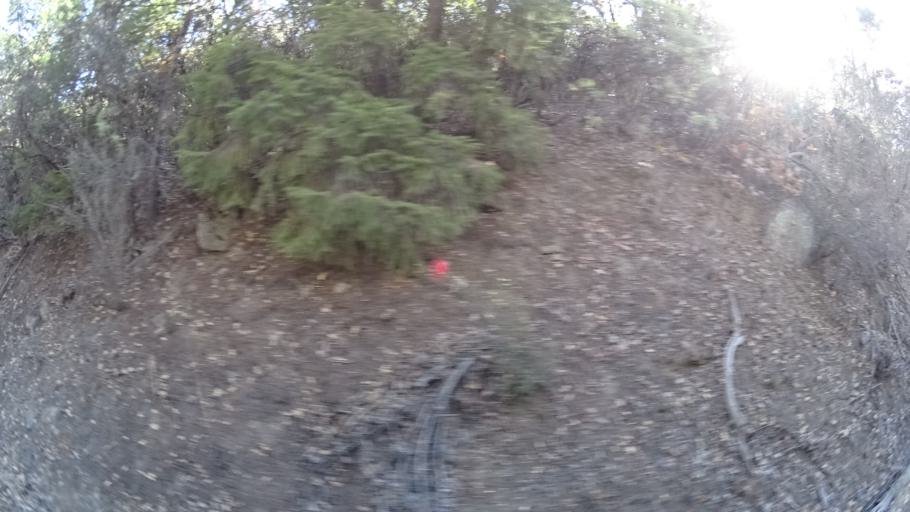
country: US
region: California
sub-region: Siskiyou County
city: Yreka
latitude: 41.8457
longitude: -122.8367
